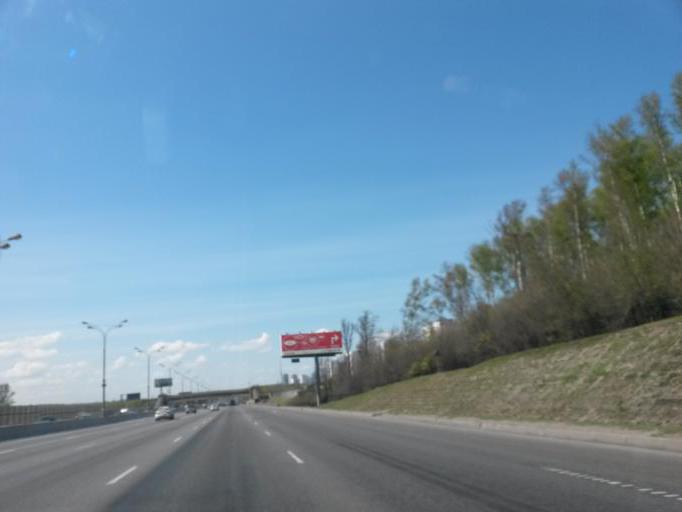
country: RU
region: Moscow
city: Yasenevo
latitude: 55.5865
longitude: 37.5507
